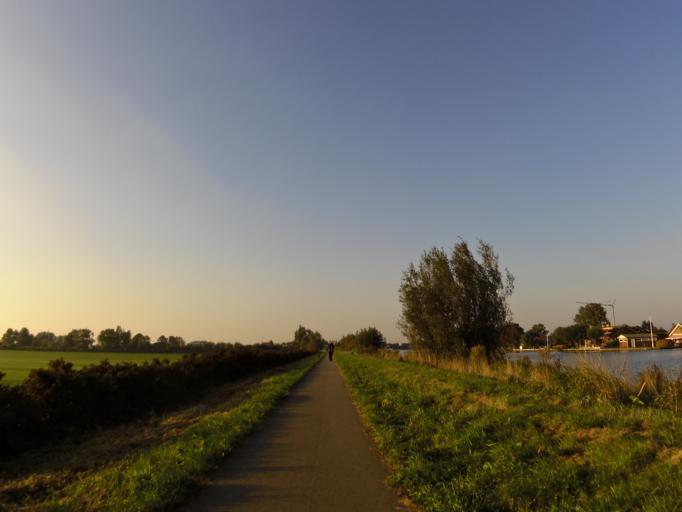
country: NL
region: South Holland
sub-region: Gemeente Kaag en Braassem
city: Oude Wetering
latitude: 52.1771
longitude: 4.6336
